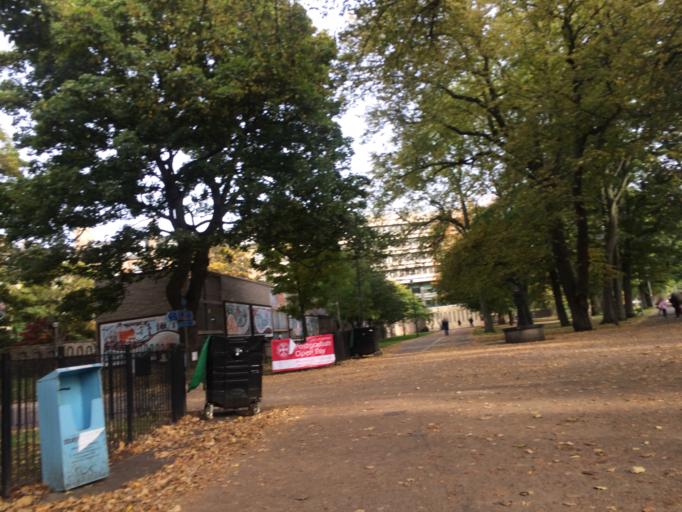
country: GB
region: Scotland
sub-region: Edinburgh
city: Edinburgh
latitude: 55.9426
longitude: -3.1917
